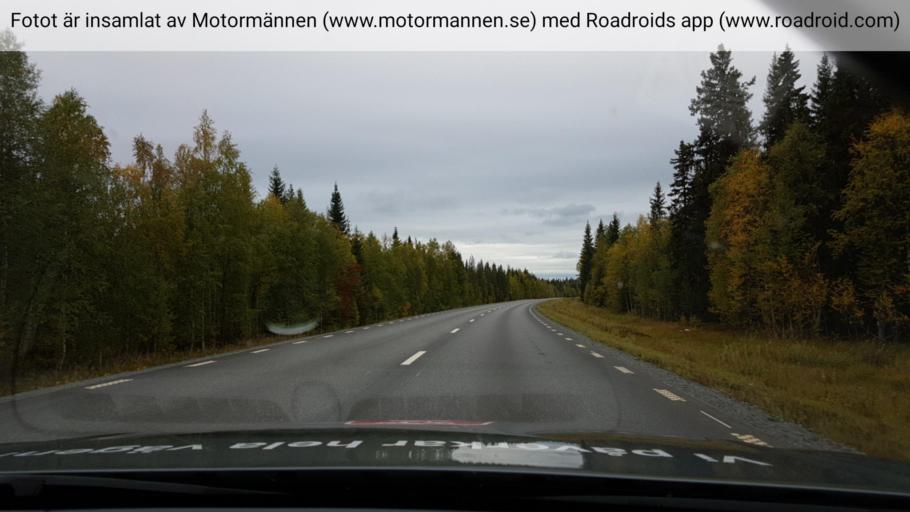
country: SE
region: Vaesterbotten
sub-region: Dorotea Kommun
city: Dorotea
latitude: 64.3111
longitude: 16.6042
